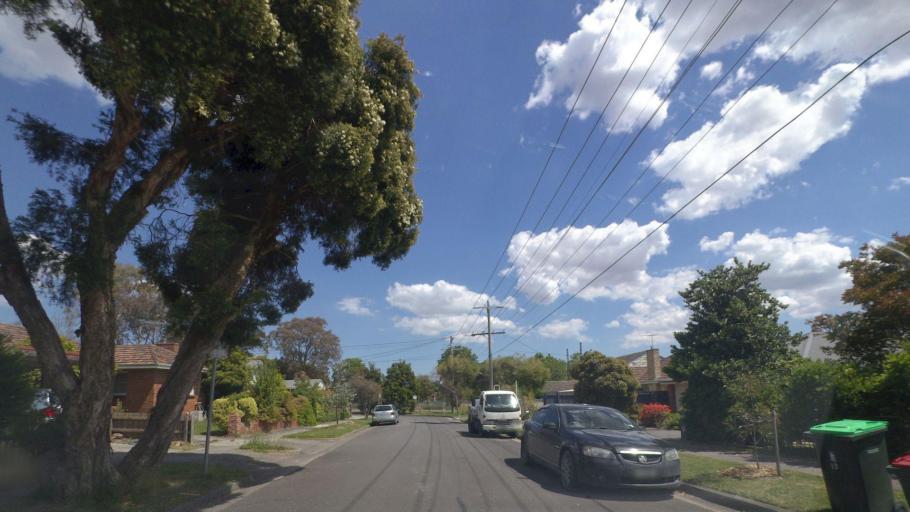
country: AU
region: Victoria
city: Mitcham
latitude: -37.8177
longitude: 145.2059
